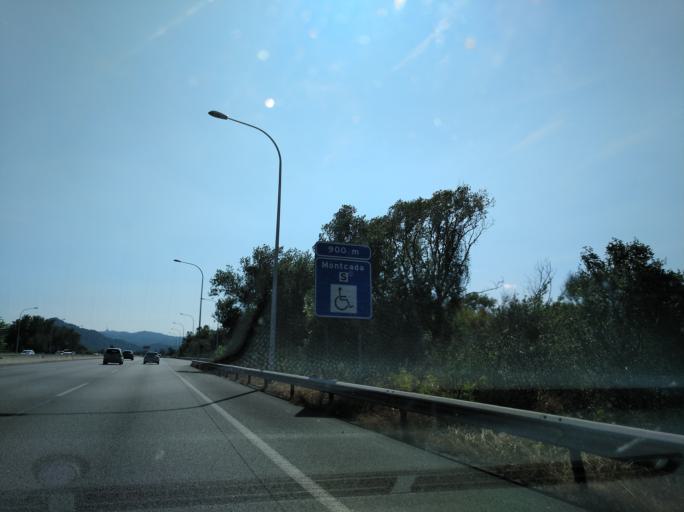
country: ES
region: Catalonia
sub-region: Provincia de Barcelona
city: La Llagosta
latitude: 41.5061
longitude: 2.2002
